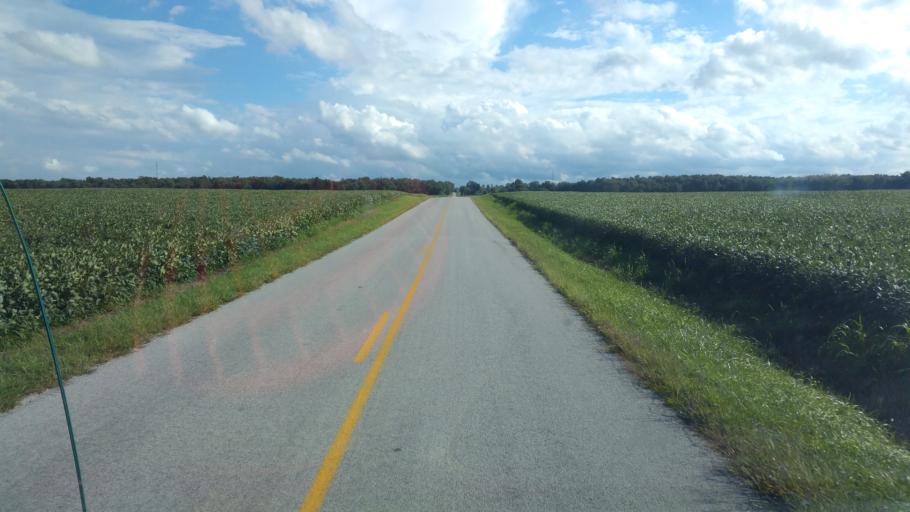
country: US
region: Ohio
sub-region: Hardin County
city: Kenton
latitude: 40.6781
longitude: -83.6337
